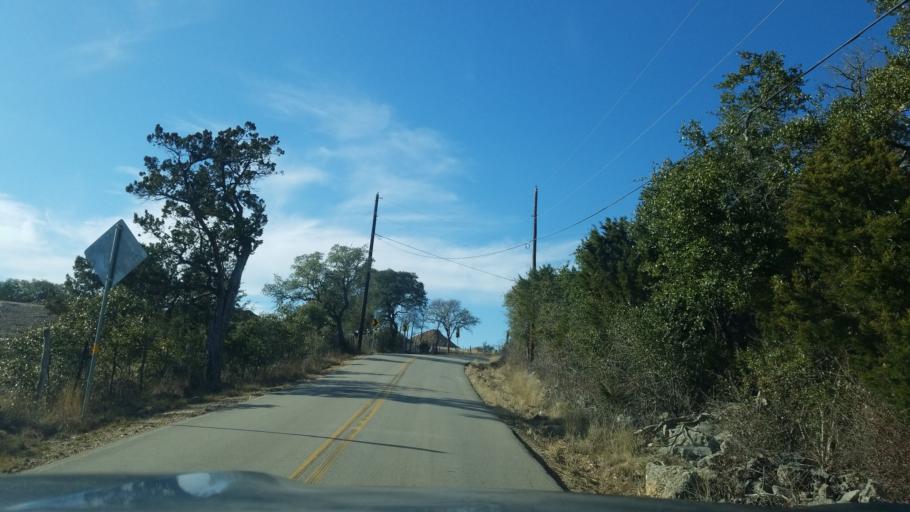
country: US
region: Texas
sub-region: Comal County
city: Canyon Lake
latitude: 29.7828
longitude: -98.2827
